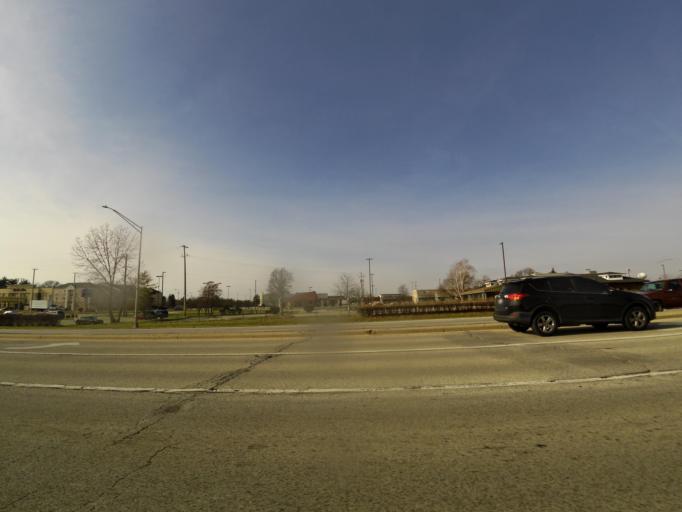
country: US
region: Illinois
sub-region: Macon County
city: Forsyth
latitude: 39.9168
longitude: -88.9553
